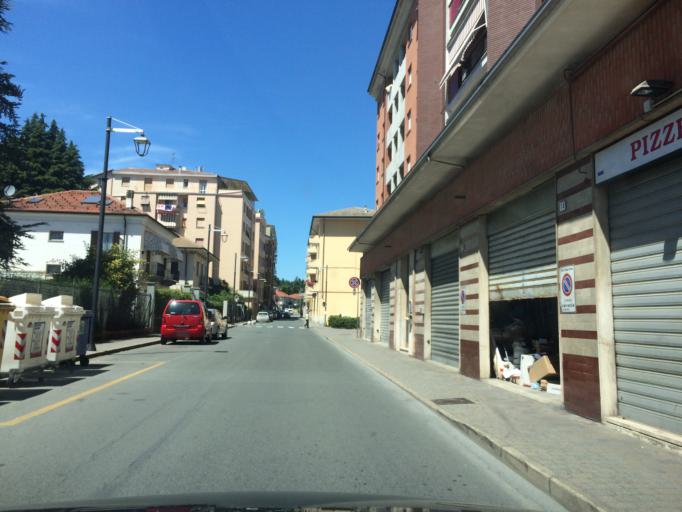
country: IT
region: Piedmont
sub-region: Provincia di Alessandria
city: Acqui Terme
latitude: 44.6768
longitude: 8.4644
